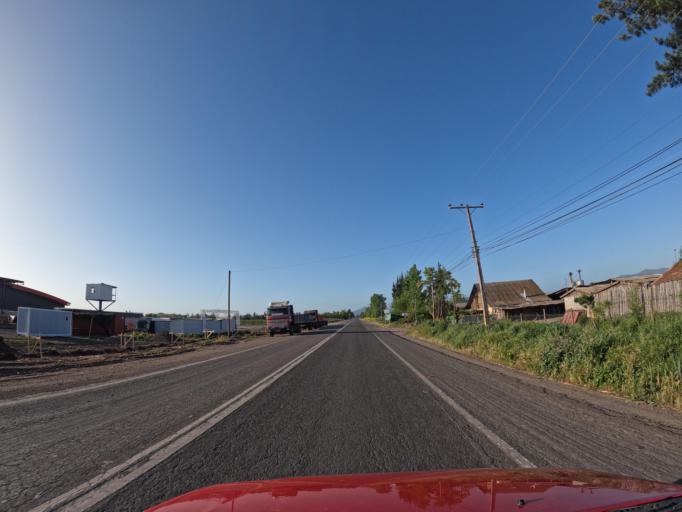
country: CL
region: O'Higgins
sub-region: Provincia de Colchagua
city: Santa Cruz
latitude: -34.5047
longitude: -71.3629
